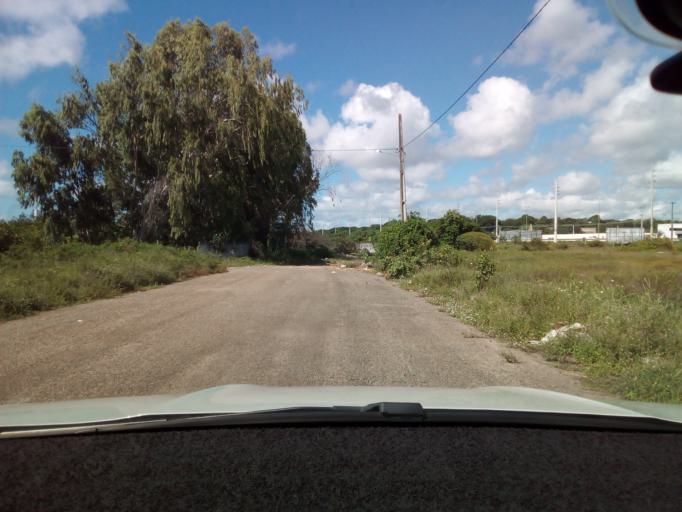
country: BR
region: Paraiba
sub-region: Joao Pessoa
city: Joao Pessoa
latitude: -7.0559
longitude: -34.8496
